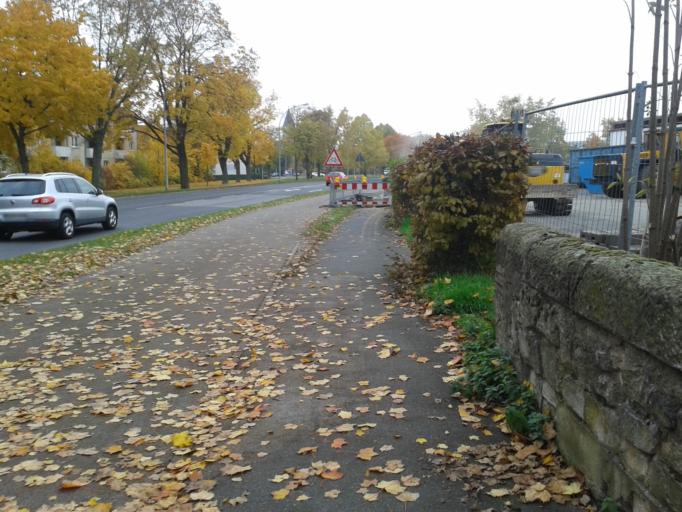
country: DE
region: Bavaria
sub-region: Upper Franconia
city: Bamberg
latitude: 49.9147
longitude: 10.9157
